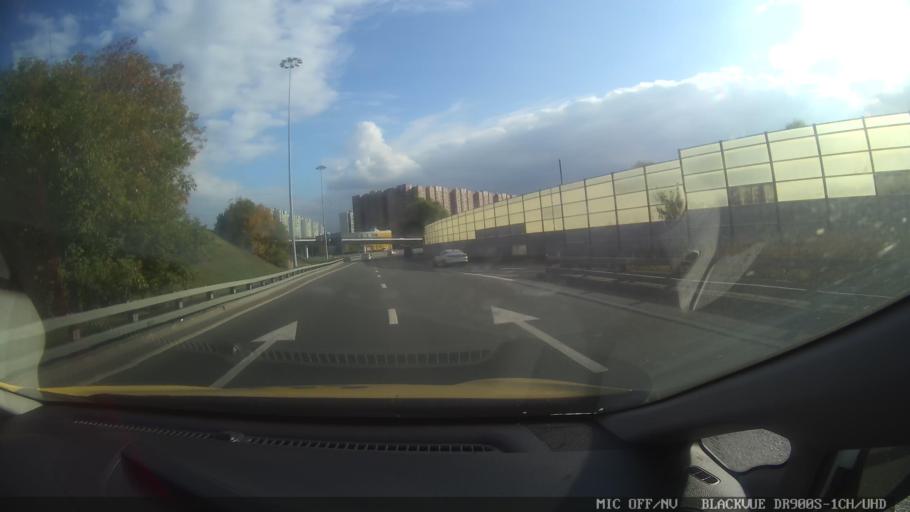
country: RU
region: Moscow
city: Yaroslavskiy
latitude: 55.8827
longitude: 37.7211
